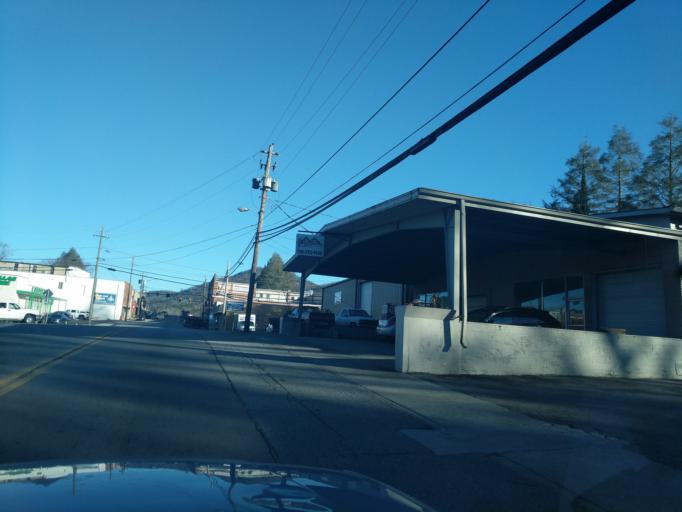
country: US
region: Georgia
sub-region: Rabun County
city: Clayton
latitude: 34.8786
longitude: -83.4033
